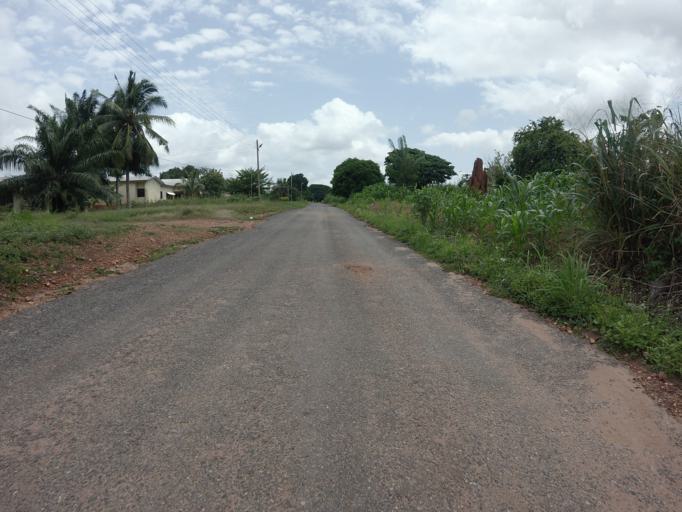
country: GH
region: Volta
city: Ho
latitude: 6.5980
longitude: 0.4826
